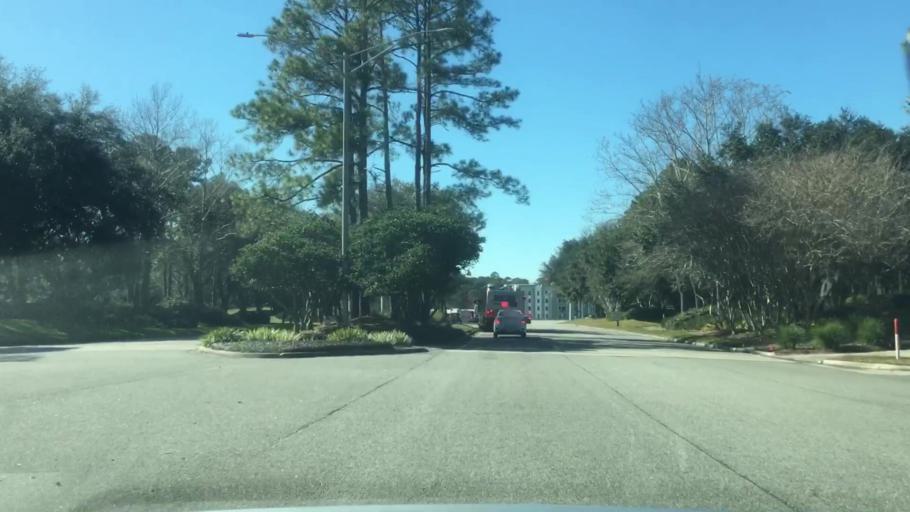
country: US
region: Florida
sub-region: Duval County
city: Jacksonville
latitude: 30.2404
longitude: -81.5498
